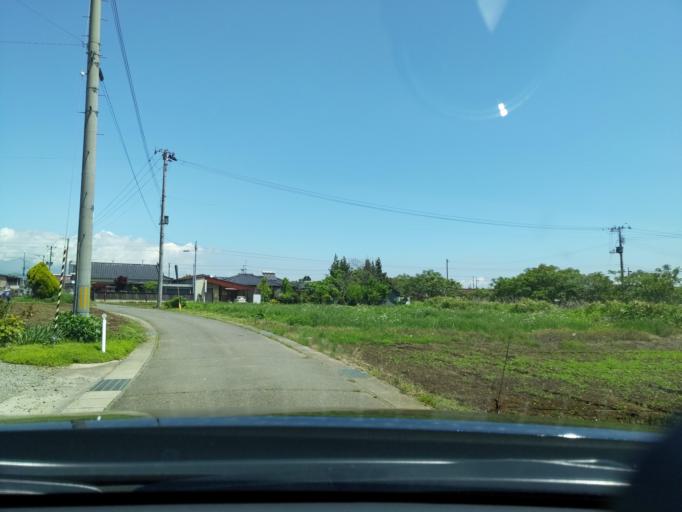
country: JP
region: Fukushima
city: Koriyama
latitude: 37.3913
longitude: 140.2861
